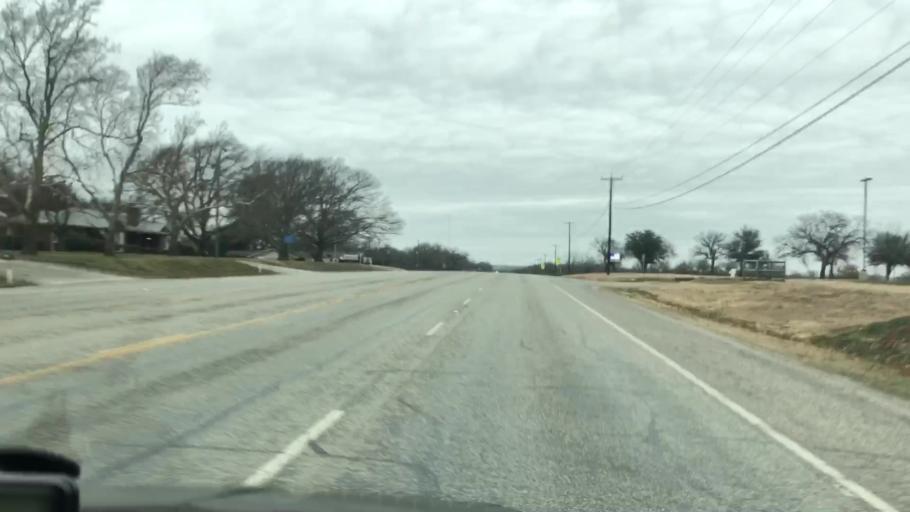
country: US
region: Texas
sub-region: Jack County
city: Jacksboro
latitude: 33.2276
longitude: -98.1682
